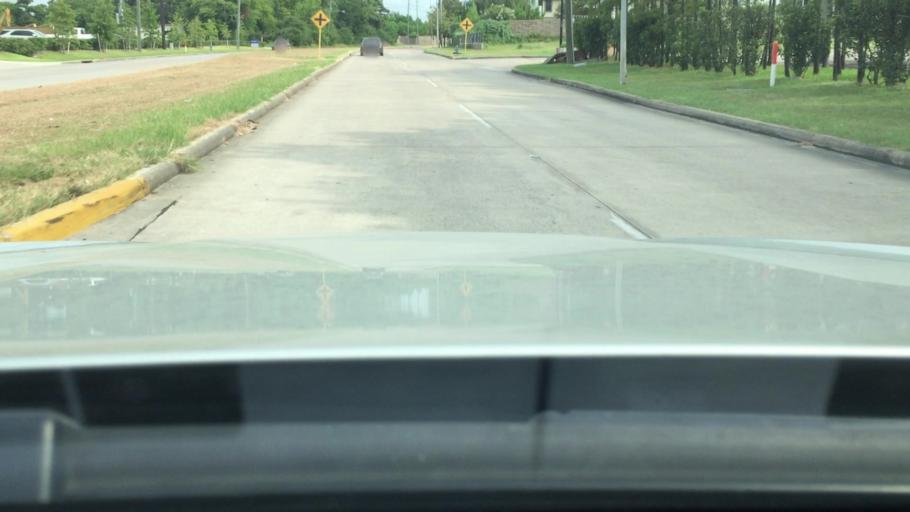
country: US
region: Texas
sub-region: Harris County
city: Jersey Village
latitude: 29.9313
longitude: -95.5449
